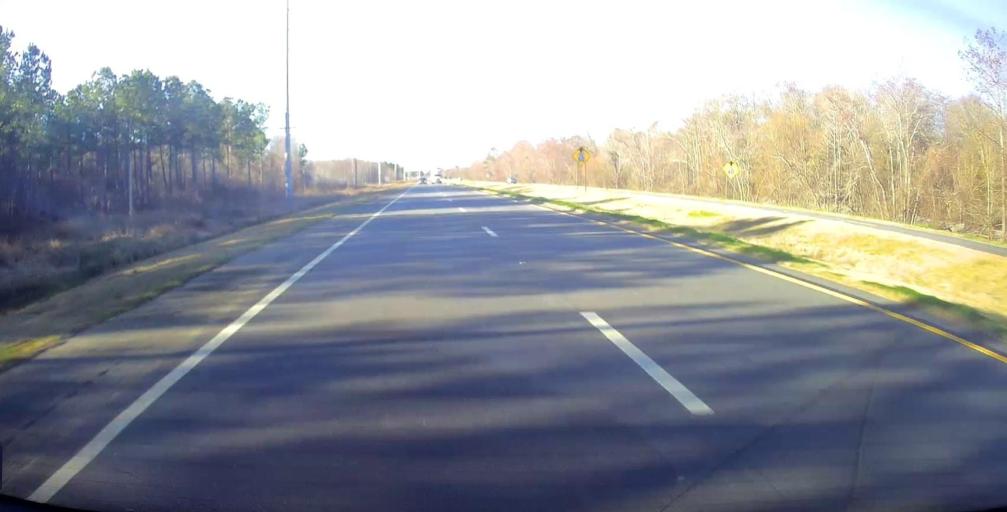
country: US
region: Georgia
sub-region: Lee County
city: Leesburg
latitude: 31.8788
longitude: -84.2419
